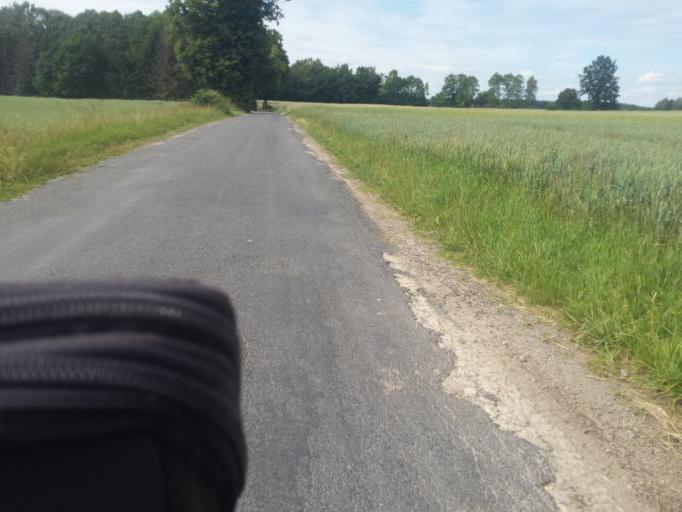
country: PL
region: Warmian-Masurian Voivodeship
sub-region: Powiat nowomiejski
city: Biskupiec
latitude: 53.5686
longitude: 19.4359
